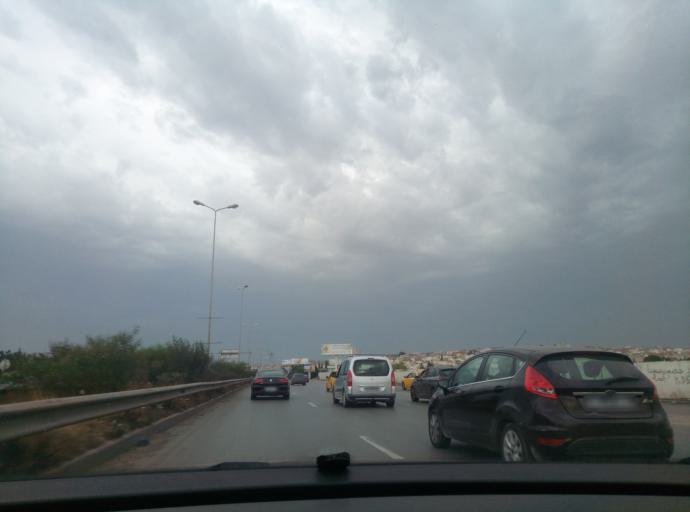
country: TN
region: Bin 'Arus
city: Ben Arous
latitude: 36.7600
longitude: 10.1992
